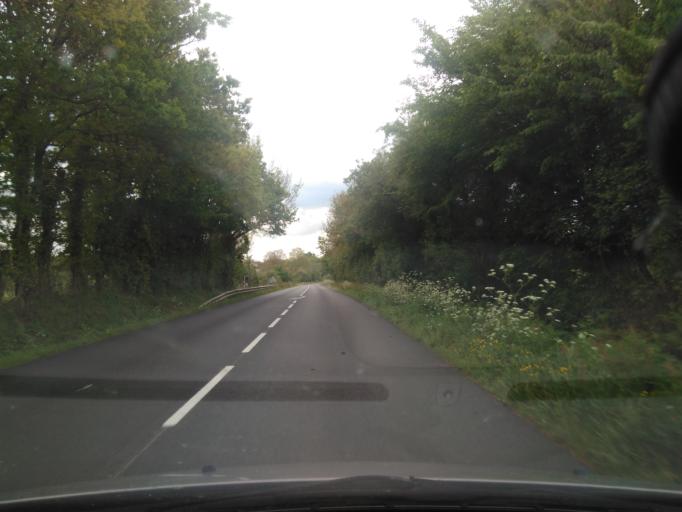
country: FR
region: Pays de la Loire
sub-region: Departement de la Vendee
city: Mouilleron-le-Captif
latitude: 46.7056
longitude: -1.4161
